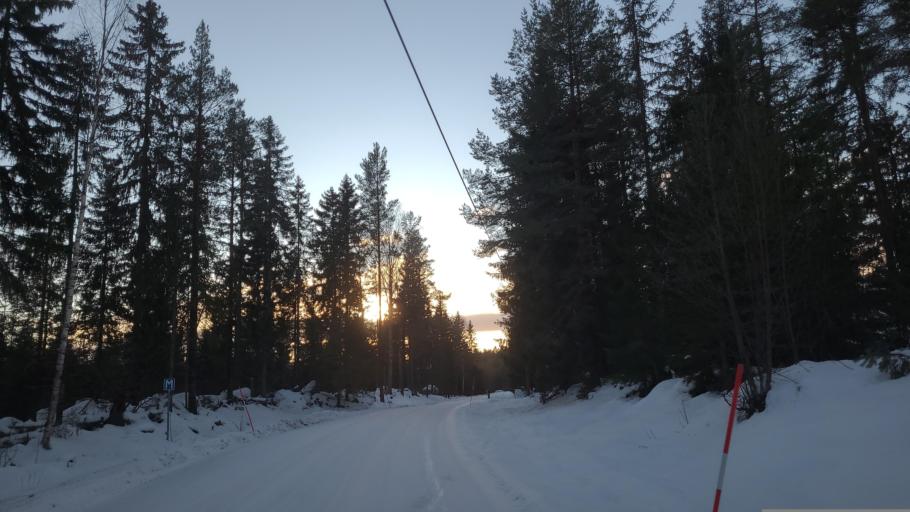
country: SE
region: Gaevleborg
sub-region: Bollnas Kommun
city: Kilafors
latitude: 61.3722
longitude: 16.6790
